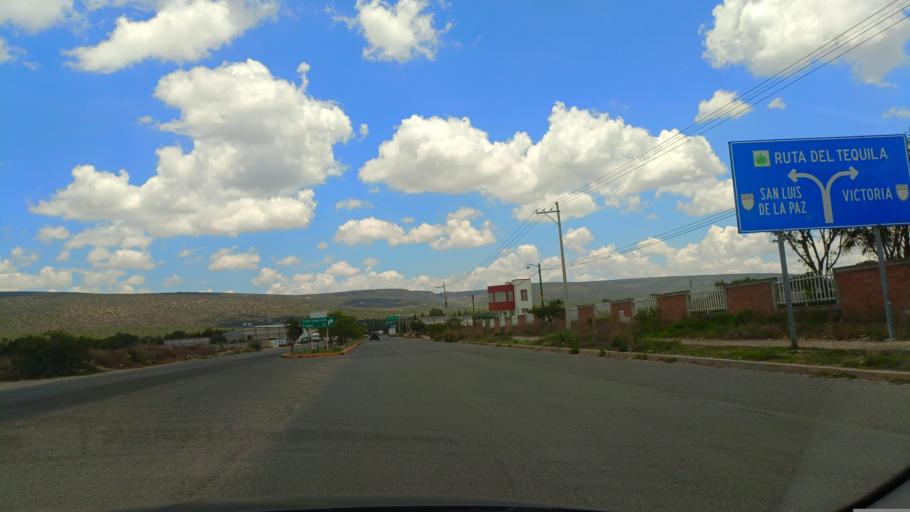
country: MX
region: Guanajuato
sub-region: San Luis de la Paz
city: San Luis de la Paz
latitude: 21.2913
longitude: -100.4907
